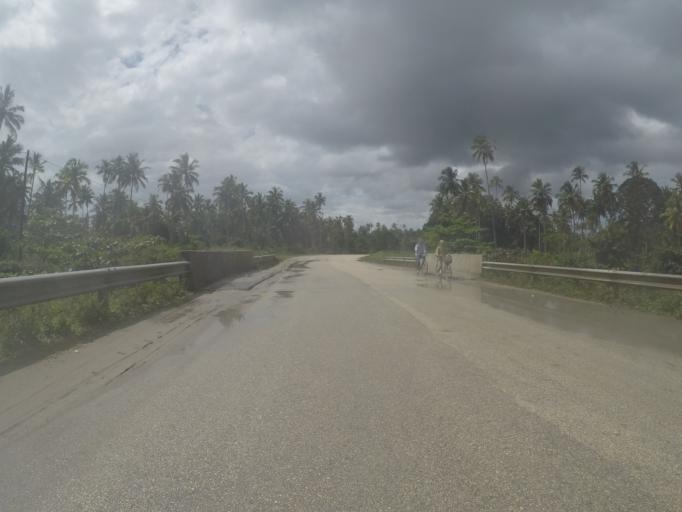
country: TZ
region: Zanzibar North
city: Gamba
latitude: -5.9792
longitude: 39.2492
